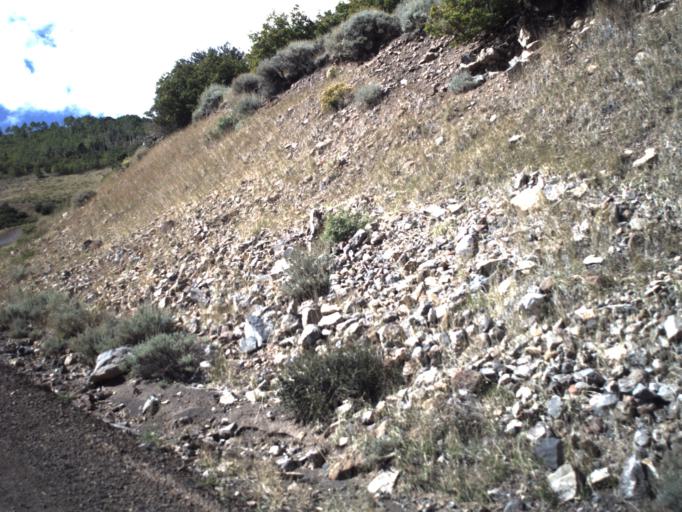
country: US
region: Utah
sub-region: Piute County
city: Junction
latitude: 38.2566
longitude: -112.3210
